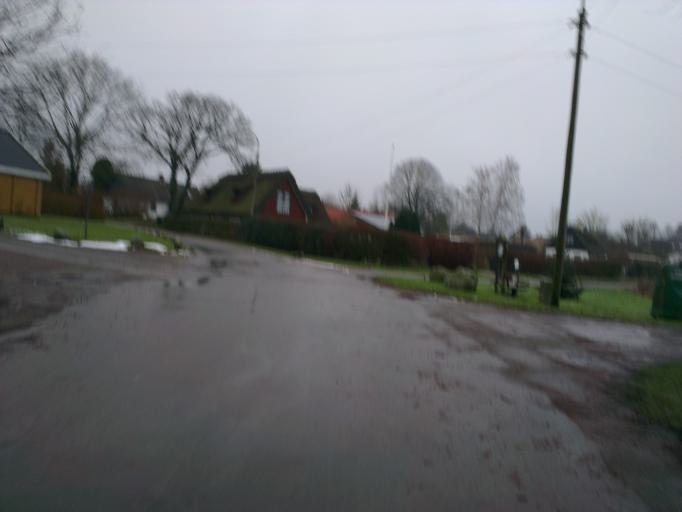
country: DK
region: Capital Region
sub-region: Frederikssund Kommune
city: Jaegerspris
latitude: 55.8362
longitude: 11.9851
